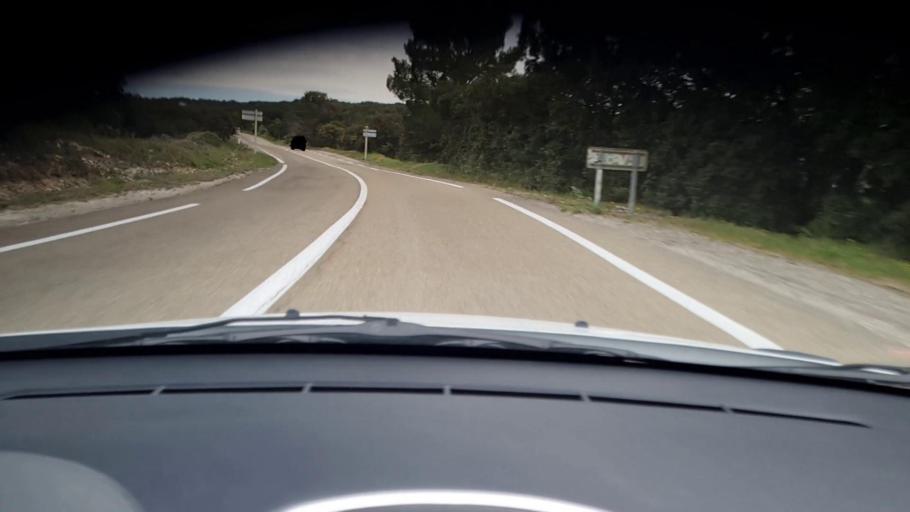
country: FR
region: Languedoc-Roussillon
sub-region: Departement du Gard
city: Poulx
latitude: 43.9170
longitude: 4.3877
